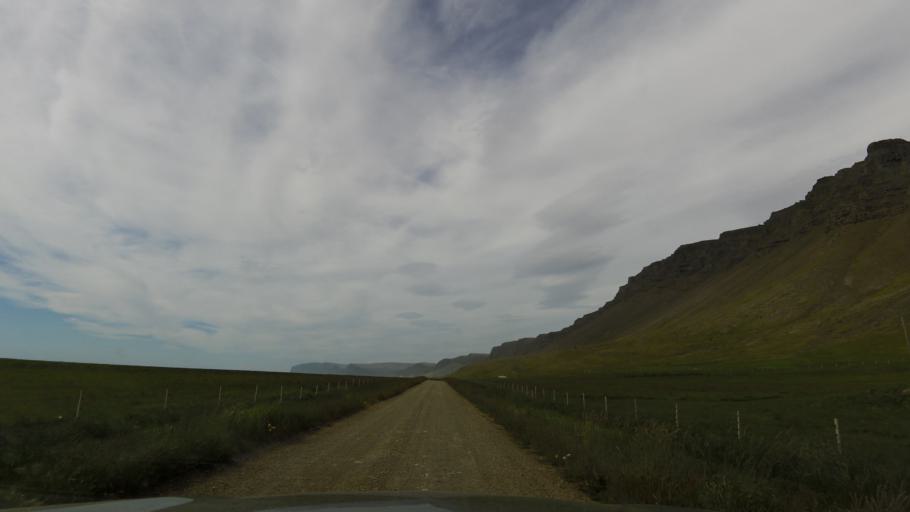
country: IS
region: West
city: Olafsvik
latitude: 65.4789
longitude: -24.0134
